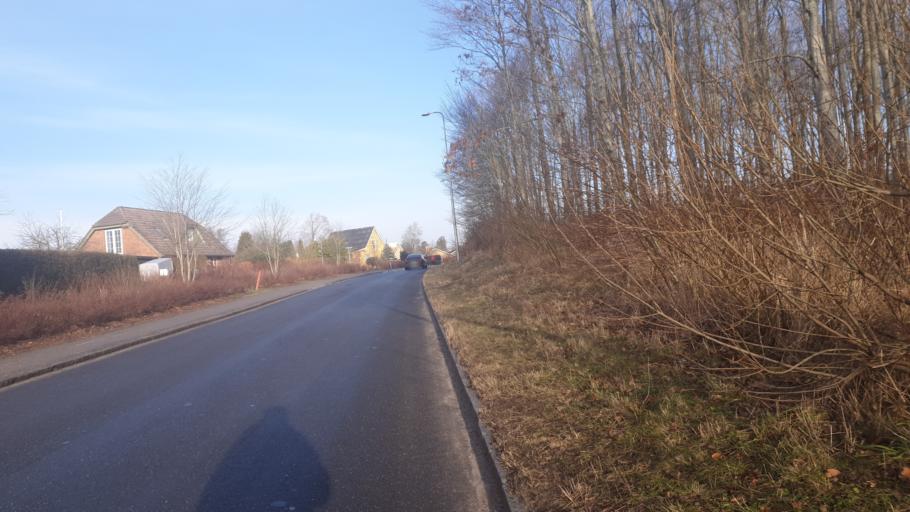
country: DK
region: Central Jutland
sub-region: Hedensted Kommune
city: Hedensted
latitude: 55.7727
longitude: 9.7187
